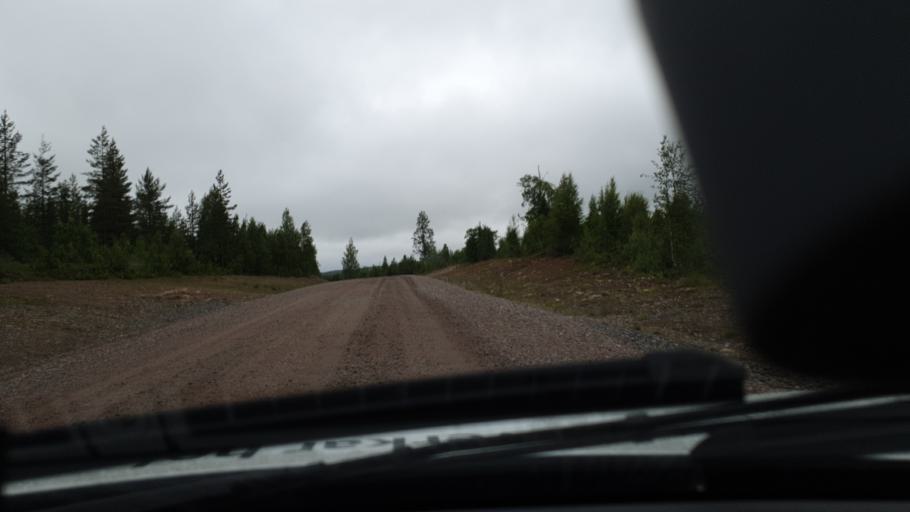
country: SE
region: Norrbotten
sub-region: Overtornea Kommun
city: OEvertornea
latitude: 66.4534
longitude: 23.4845
